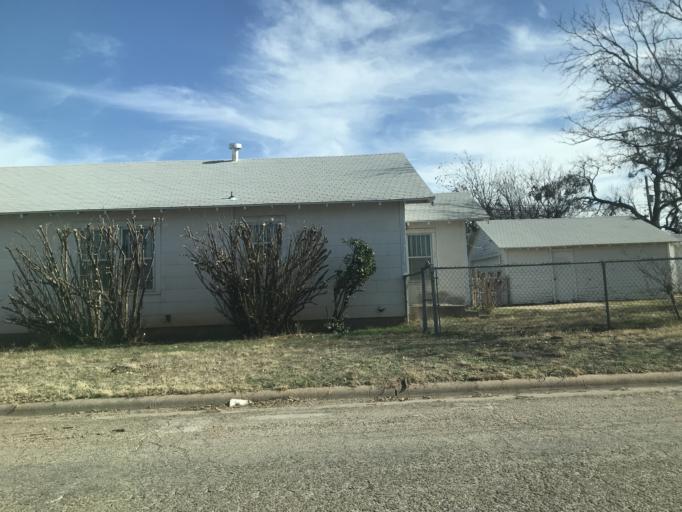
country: US
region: Texas
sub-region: Taylor County
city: Abilene
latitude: 32.4229
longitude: -99.7557
